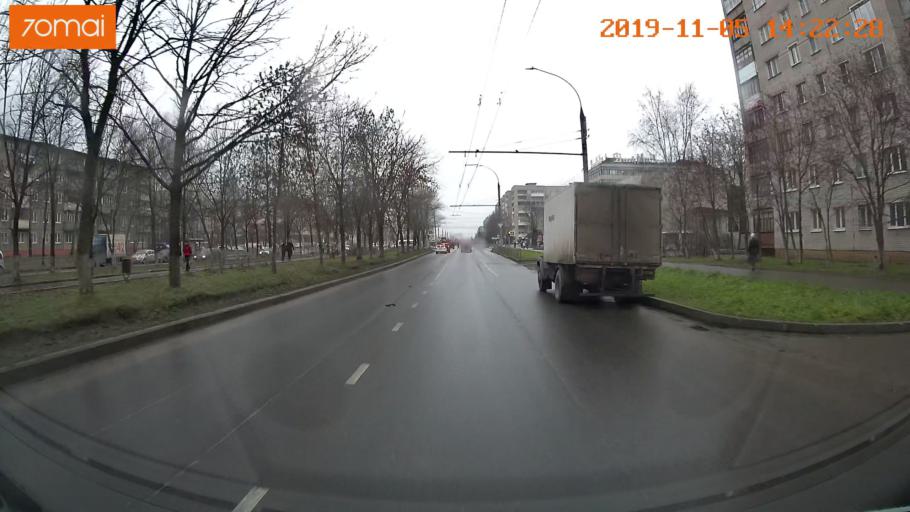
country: RU
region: Ivanovo
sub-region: Gorod Ivanovo
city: Ivanovo
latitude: 56.9639
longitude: 41.0040
